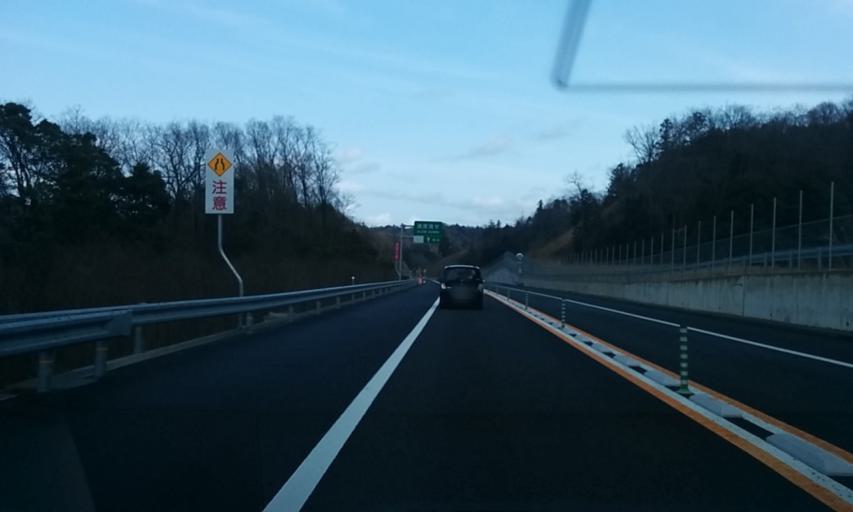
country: JP
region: Kyoto
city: Miyazu
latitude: 35.5708
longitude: 135.1211
